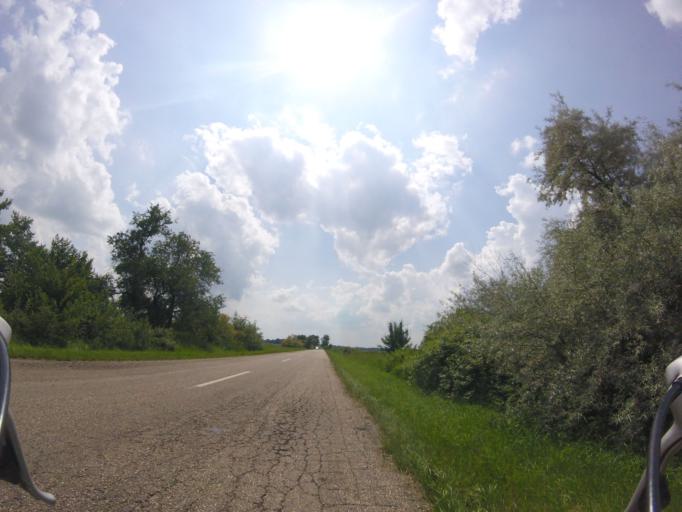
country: HU
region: Heves
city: Tiszanana
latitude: 47.5796
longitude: 20.4270
